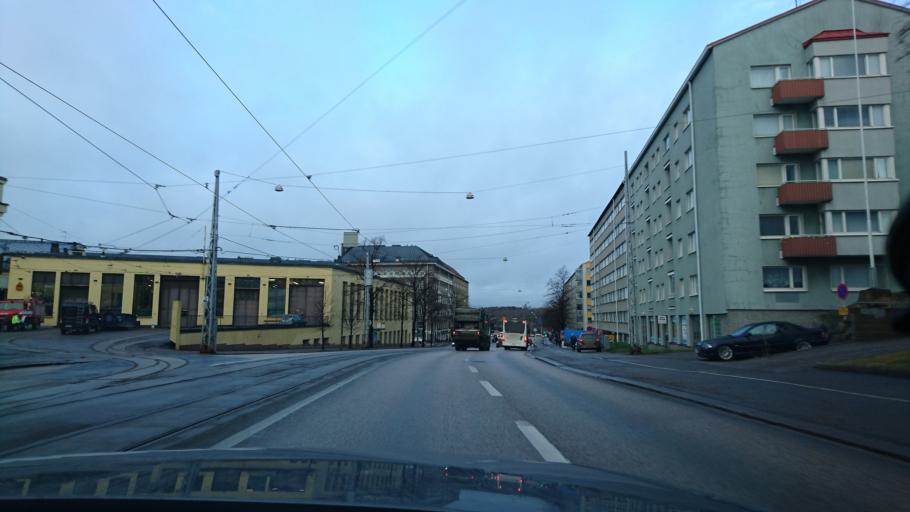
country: FI
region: Uusimaa
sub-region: Helsinki
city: Helsinki
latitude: 60.1948
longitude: 24.9635
